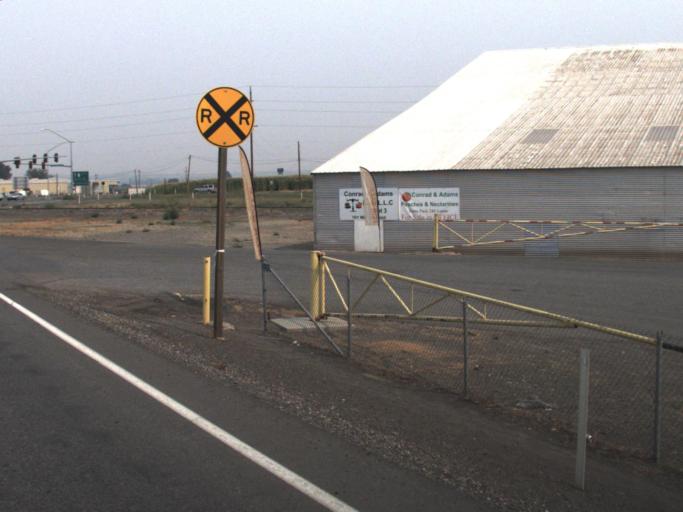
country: US
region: Washington
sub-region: Yakima County
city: Sunnyside
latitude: 46.3113
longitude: -119.9787
